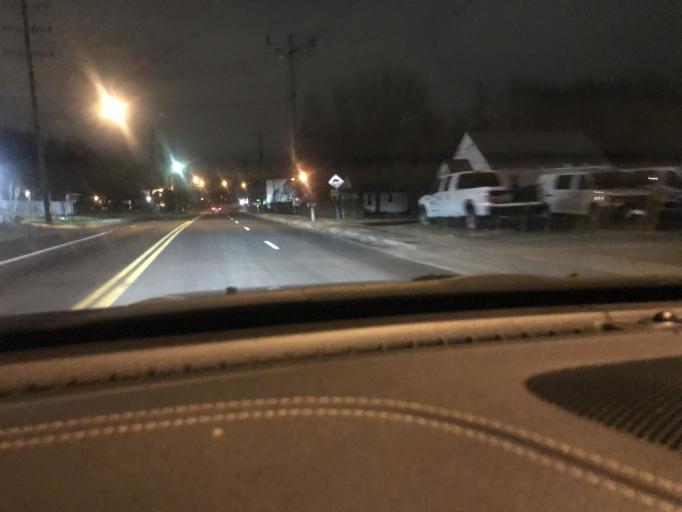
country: US
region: Maryland
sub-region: Prince George's County
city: Oxon Hill
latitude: 38.7966
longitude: -76.9839
